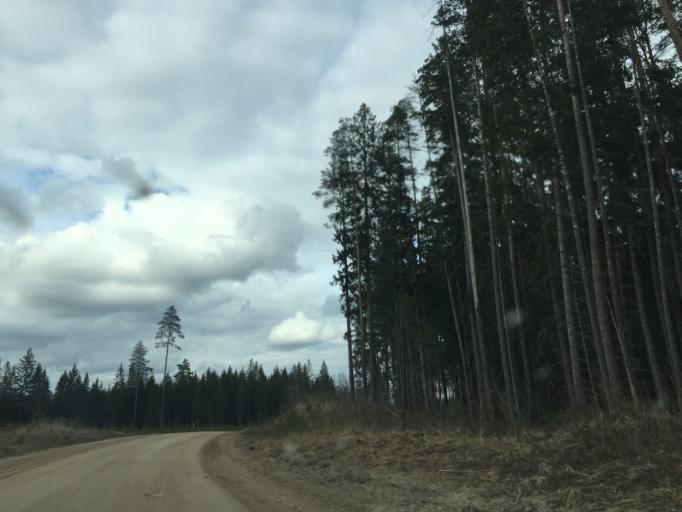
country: LV
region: Lielvarde
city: Lielvarde
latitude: 56.5448
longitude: 24.8432
